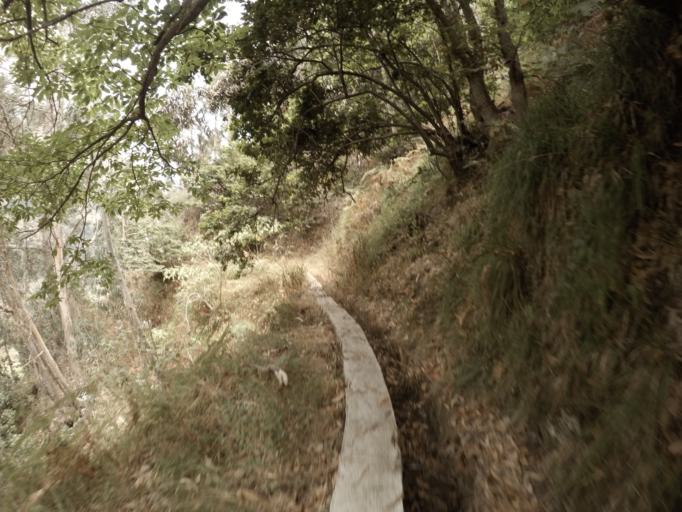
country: PT
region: Madeira
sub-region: Camara de Lobos
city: Curral das Freiras
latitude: 32.6848
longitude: -16.9624
